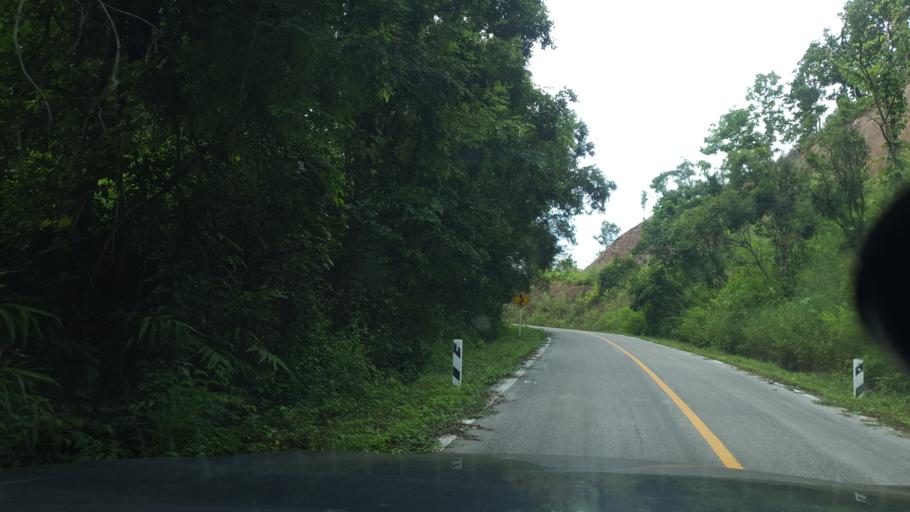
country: TH
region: Lamphun
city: Mae Tha
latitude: 18.4949
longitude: 99.2673
